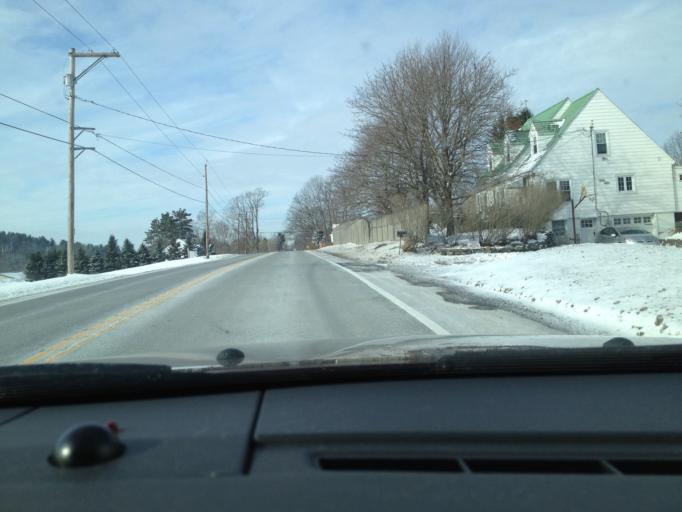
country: US
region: New York
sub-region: Rensselaer County
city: West Sand Lake
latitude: 42.6431
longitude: -73.6263
